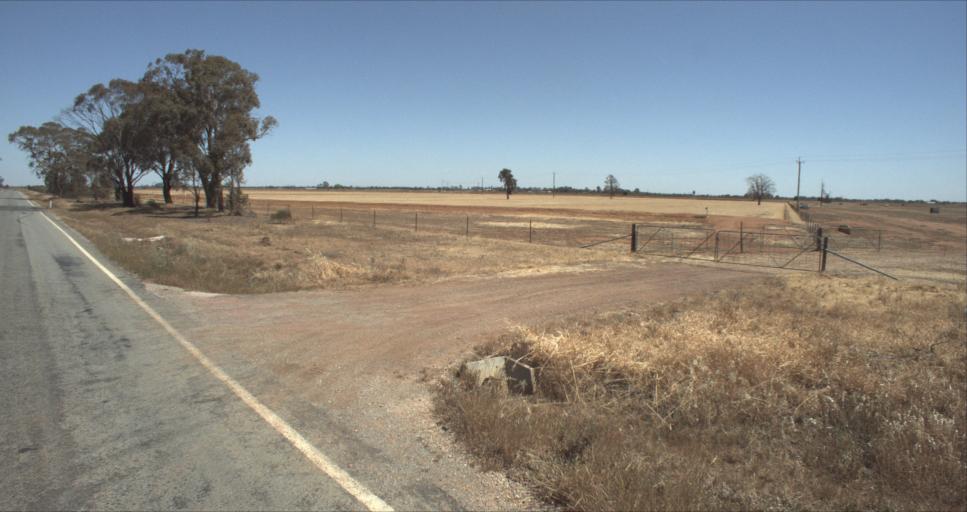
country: AU
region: New South Wales
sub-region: Leeton
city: Leeton
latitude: -34.4876
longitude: 146.4330
